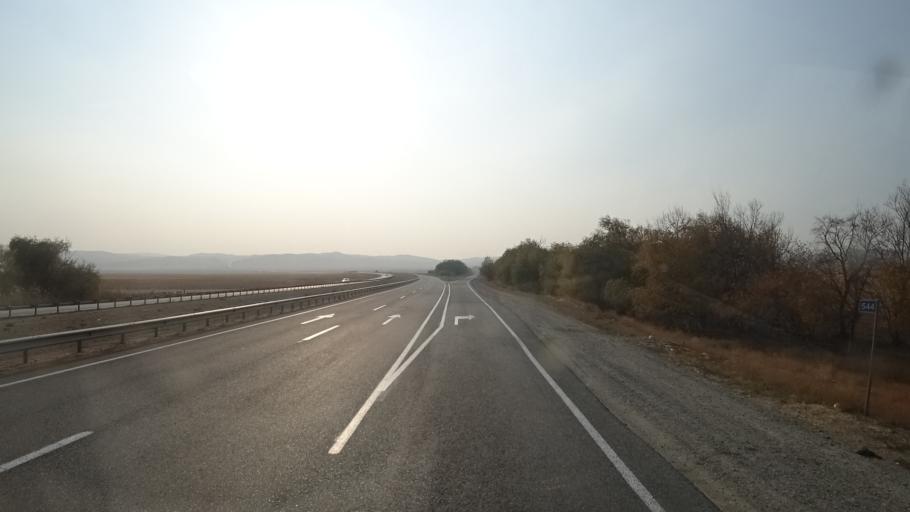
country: KZ
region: Zhambyl
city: Taraz
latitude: 42.7866
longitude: 71.0542
